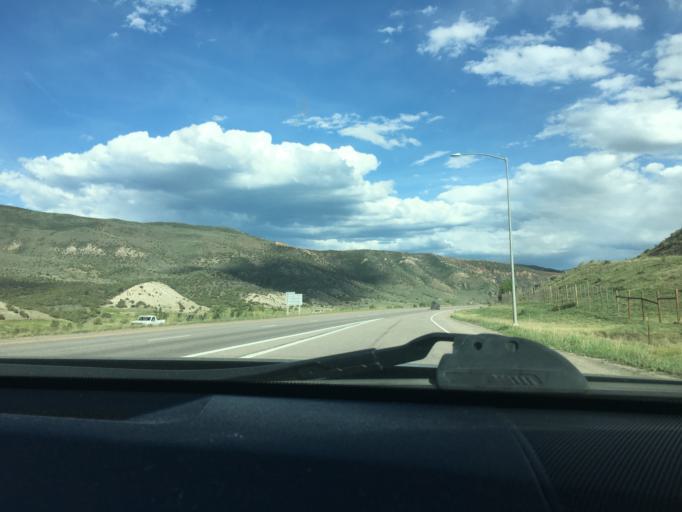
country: US
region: Colorado
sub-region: Eagle County
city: Edwards
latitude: 39.6953
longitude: -106.6681
